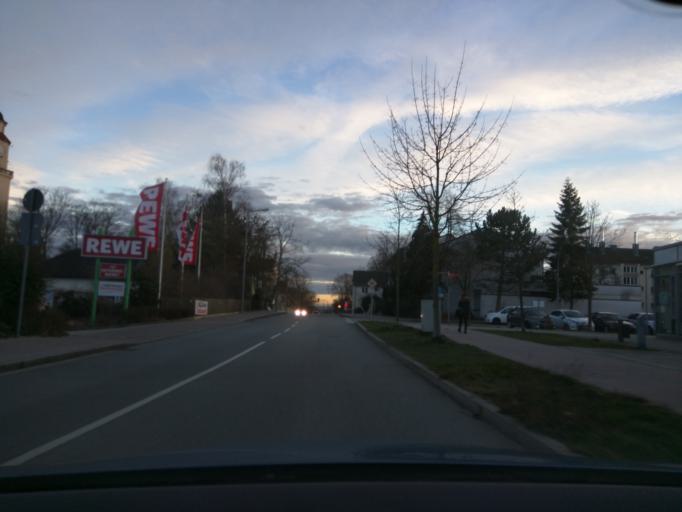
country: DE
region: Bavaria
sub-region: Upper Bavaria
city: Freising
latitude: 48.4078
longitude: 11.7375
